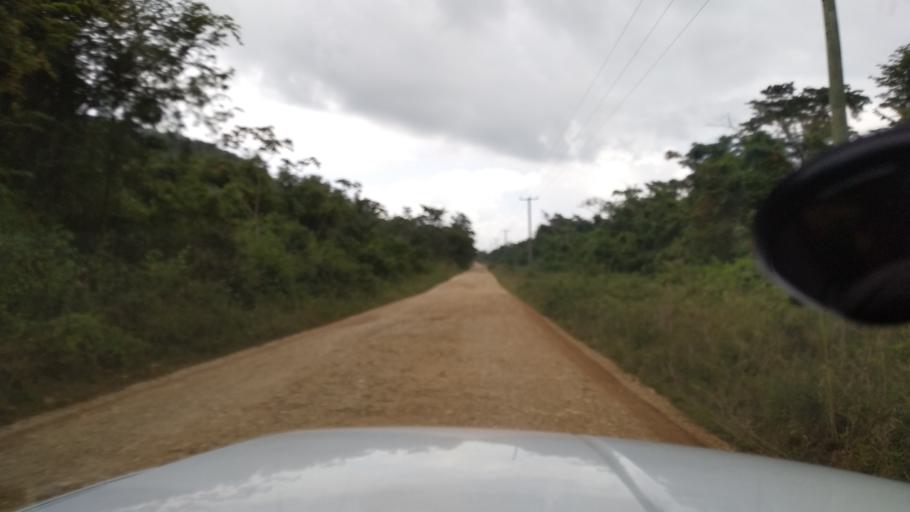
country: BZ
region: Toledo
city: Punta Gorda
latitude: 16.2135
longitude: -89.0148
